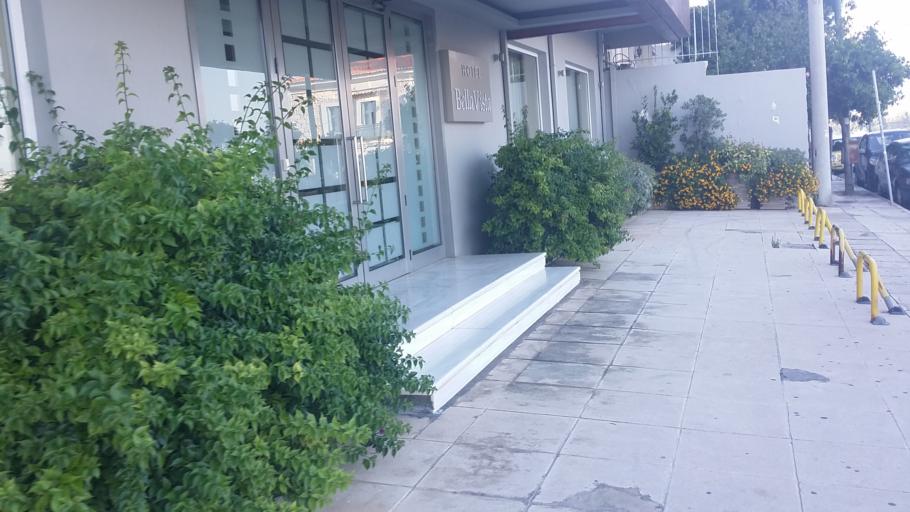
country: GR
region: Attica
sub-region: Nomarchia Athinas
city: Moskhaton
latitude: 37.9395
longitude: 23.6615
